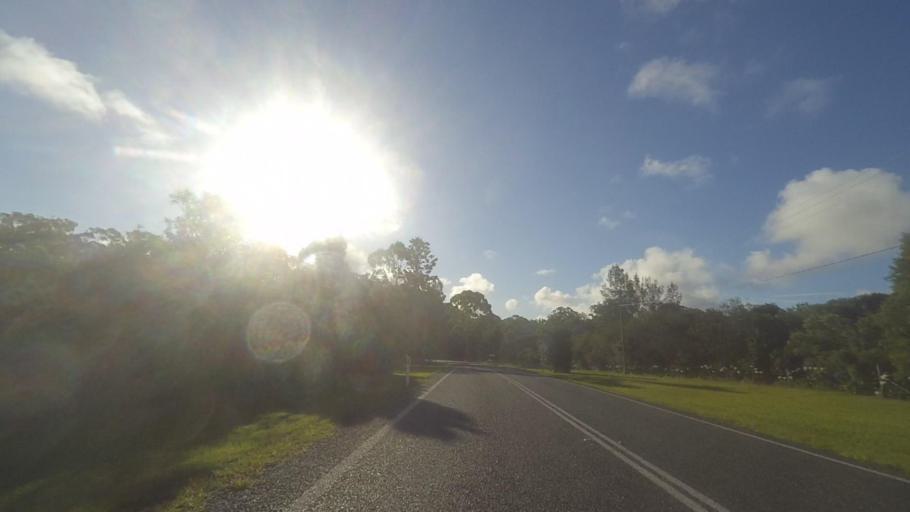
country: AU
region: New South Wales
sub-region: Great Lakes
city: Nabiac
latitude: -32.0912
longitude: 152.4448
